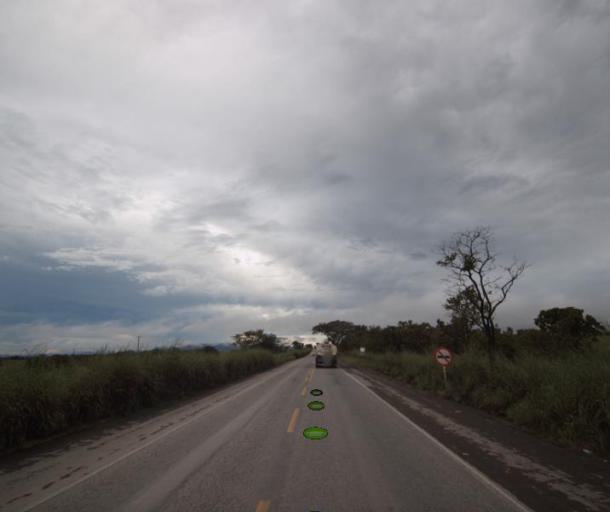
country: BR
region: Goias
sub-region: Porangatu
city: Porangatu
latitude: -13.5236
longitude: -49.1158
